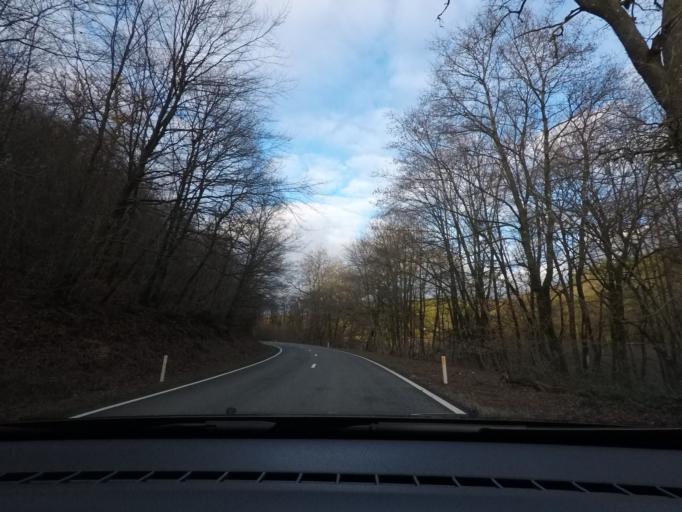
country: BE
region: Wallonia
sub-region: Province du Luxembourg
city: Tintigny
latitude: 49.7405
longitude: 5.5272
